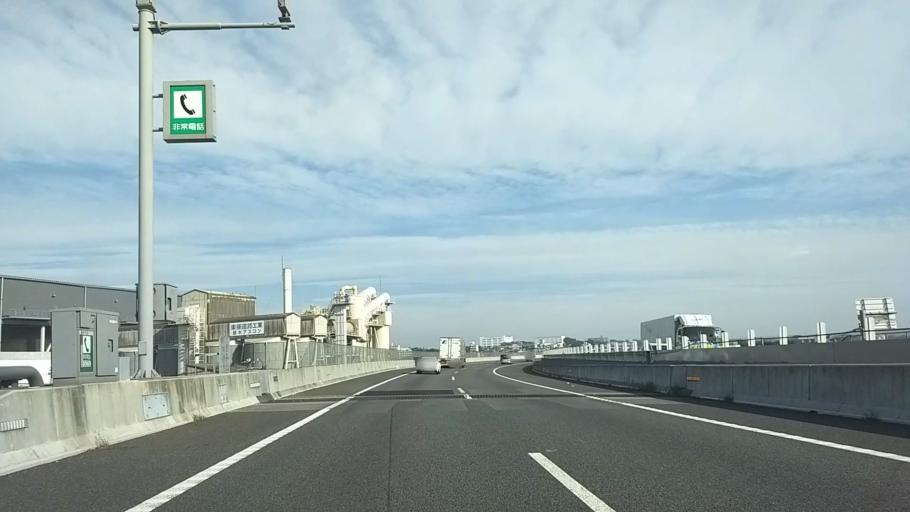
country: JP
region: Kanagawa
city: Atsugi
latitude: 35.4558
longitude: 139.3727
